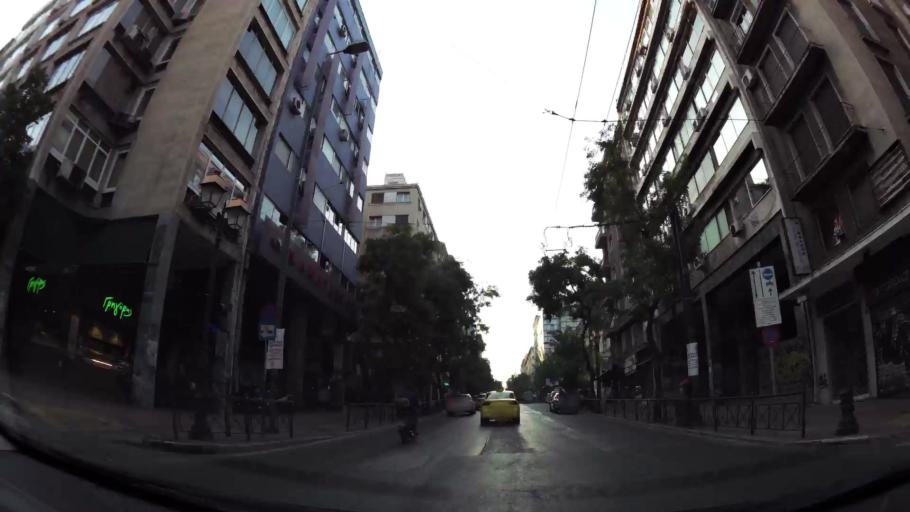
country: GR
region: Attica
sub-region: Nomarchia Athinas
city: Athens
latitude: 37.9840
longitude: 23.7322
